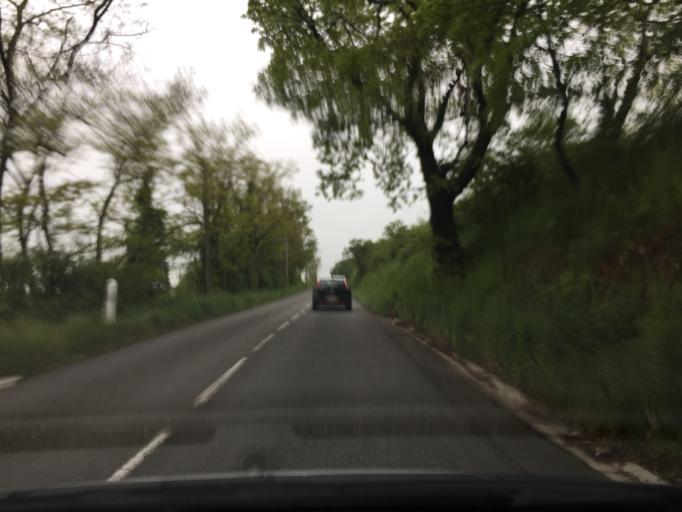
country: FR
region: Rhone-Alpes
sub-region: Departement du Rhone
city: Mornant
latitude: 45.6113
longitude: 4.6722
